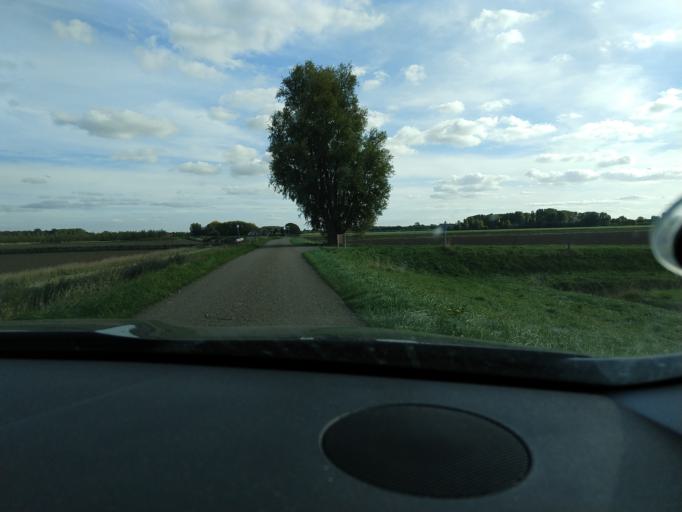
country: NL
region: Zeeland
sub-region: Gemeente Noord-Beveland
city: Kamperland
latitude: 51.5712
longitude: 3.6796
